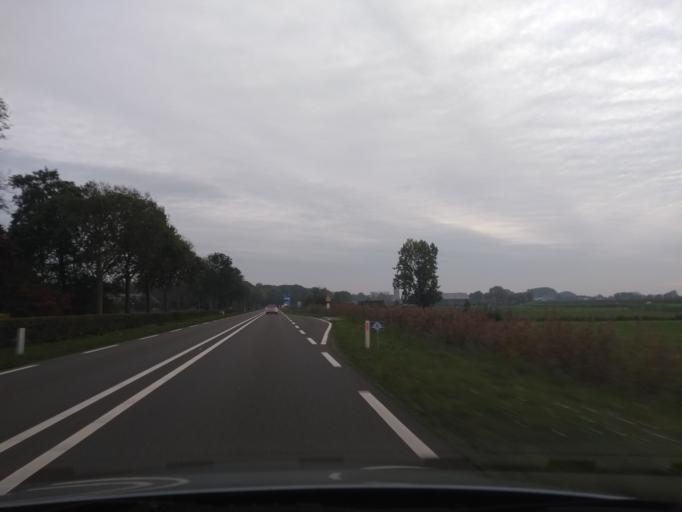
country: NL
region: Overijssel
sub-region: Gemeente Zwartewaterland
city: Hasselt
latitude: 52.6002
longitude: 6.0970
